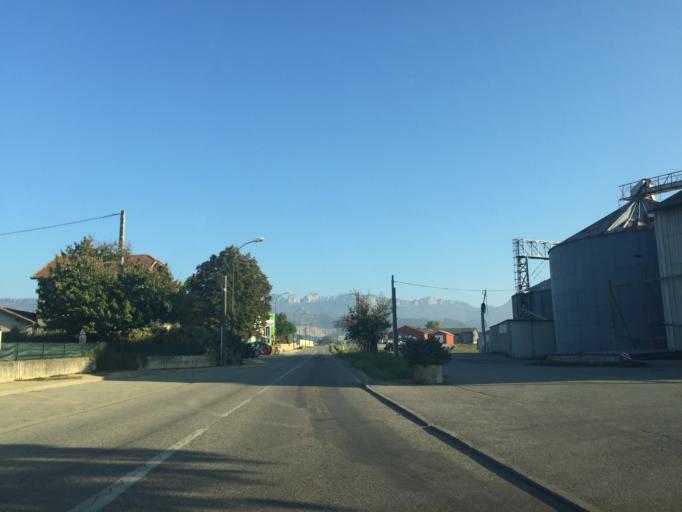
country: FR
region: Rhone-Alpes
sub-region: Departement de la Drome
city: Chatuzange-le-Goubet
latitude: 44.9890
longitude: 5.1027
